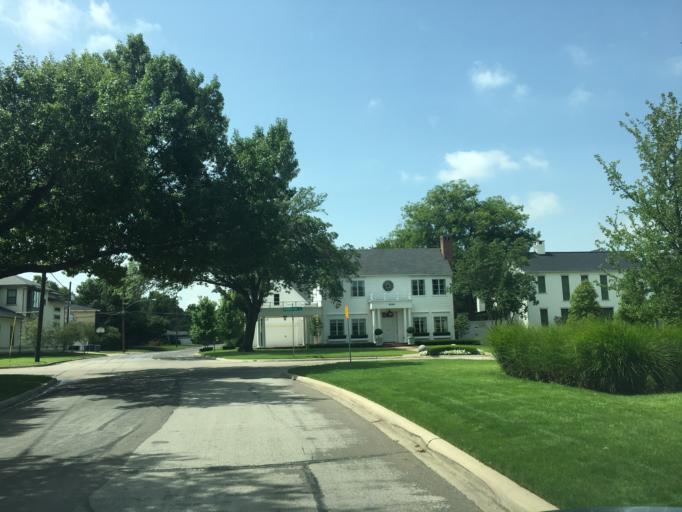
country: US
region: Texas
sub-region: Dallas County
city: University Park
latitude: 32.8919
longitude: -96.7966
